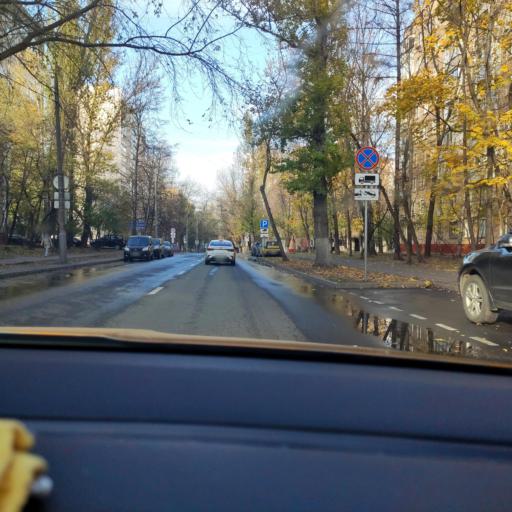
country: RU
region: Moscow
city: Tekstil'shchiki
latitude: 55.6952
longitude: 37.7439
